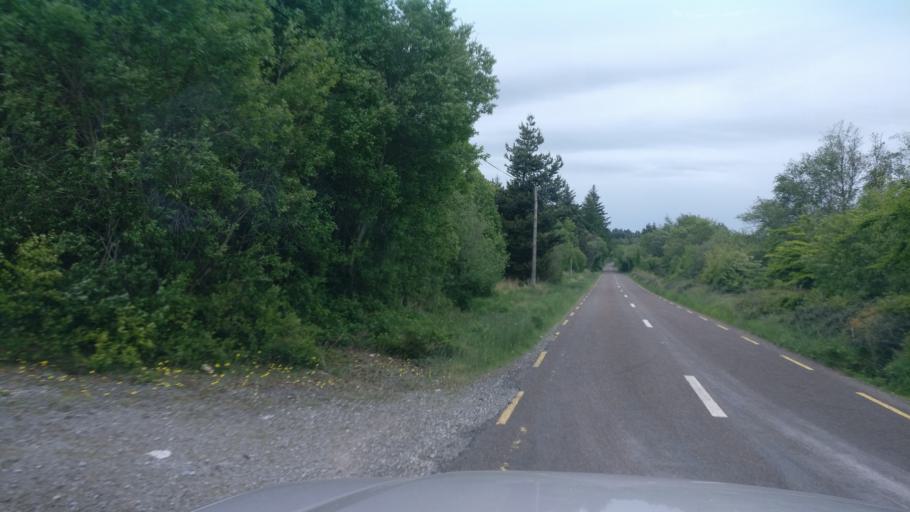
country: IE
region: Connaught
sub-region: County Galway
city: Loughrea
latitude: 53.0828
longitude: -8.5210
